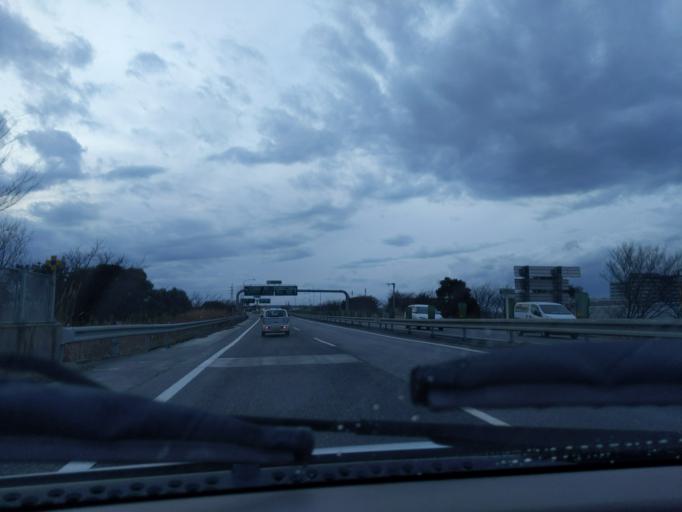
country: JP
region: Niigata
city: Niigata-shi
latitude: 37.8733
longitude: 139.0486
